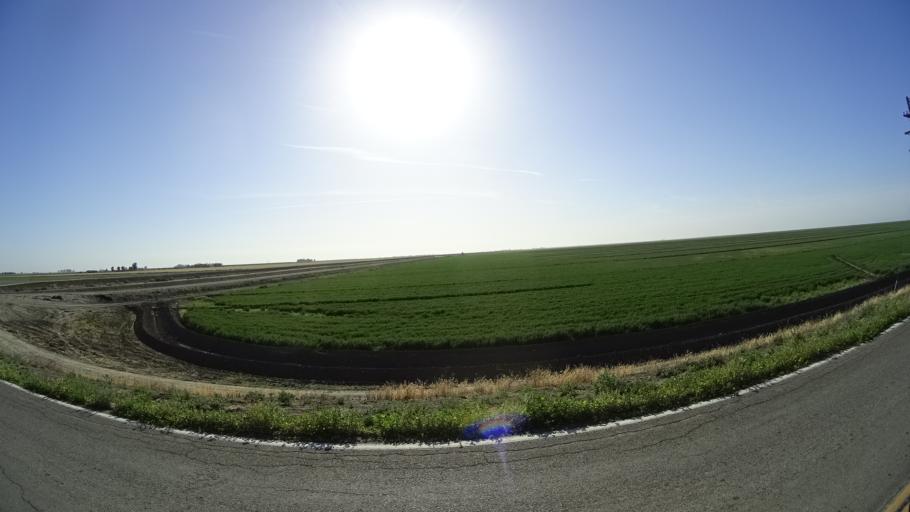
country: US
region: California
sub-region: Kings County
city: Stratford
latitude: 36.1532
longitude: -119.7980
